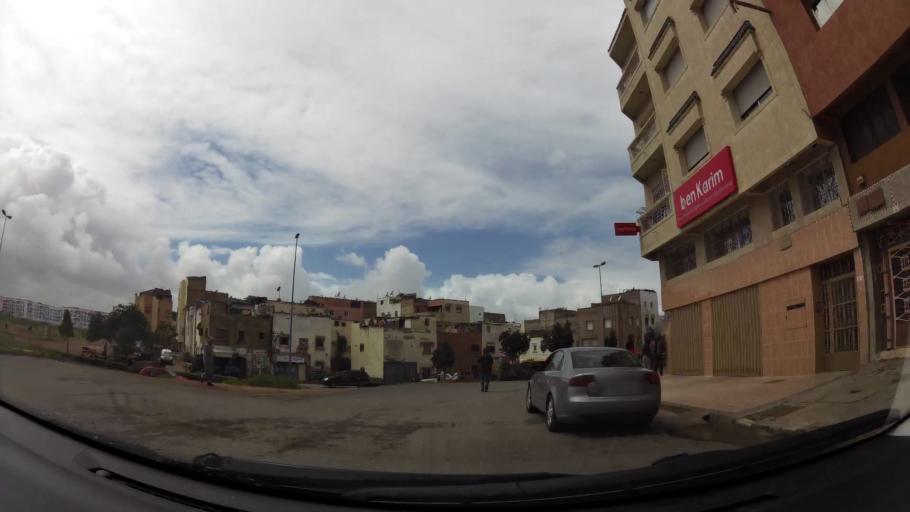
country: MA
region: Grand Casablanca
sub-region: Casablanca
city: Casablanca
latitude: 33.5493
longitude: -7.6878
